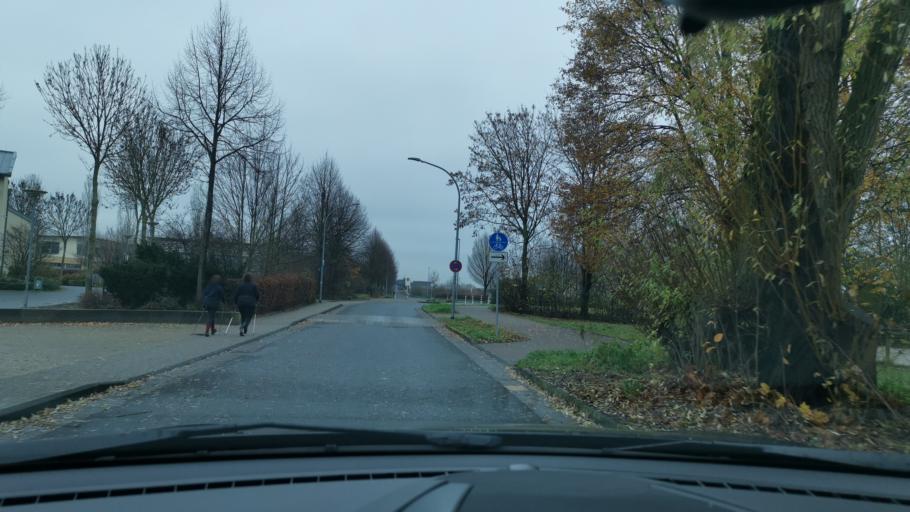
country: DE
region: North Rhine-Westphalia
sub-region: Regierungsbezirk Dusseldorf
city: Juchen
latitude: 51.1043
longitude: 6.5140
